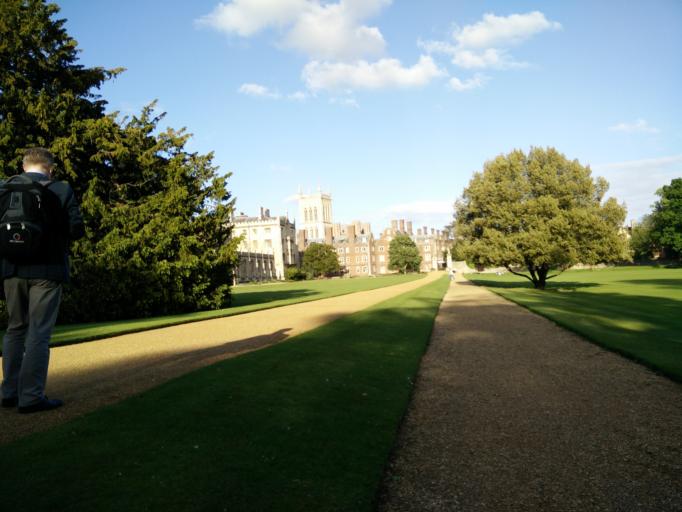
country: GB
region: England
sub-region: Cambridgeshire
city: Cambridge
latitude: 52.2084
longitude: 0.1134
